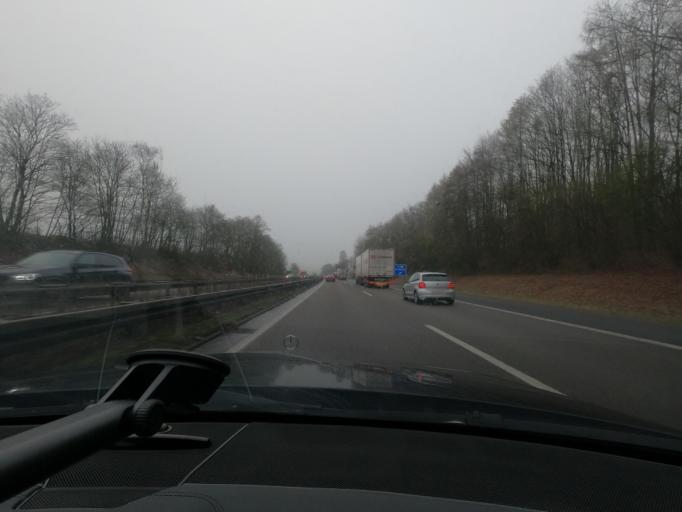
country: DE
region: Hesse
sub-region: Regierungsbezirk Kassel
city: Martinhagen
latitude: 51.3138
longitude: 9.2915
